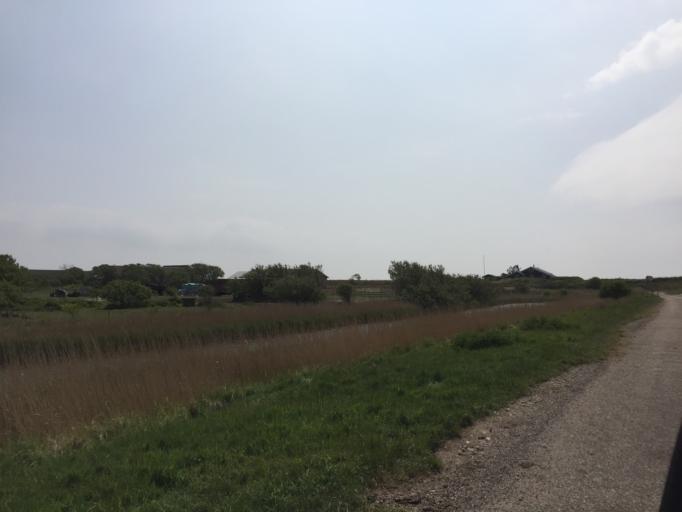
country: DK
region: South Denmark
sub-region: Esbjerg Kommune
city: Tjaereborg
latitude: 55.2832
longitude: 8.5445
